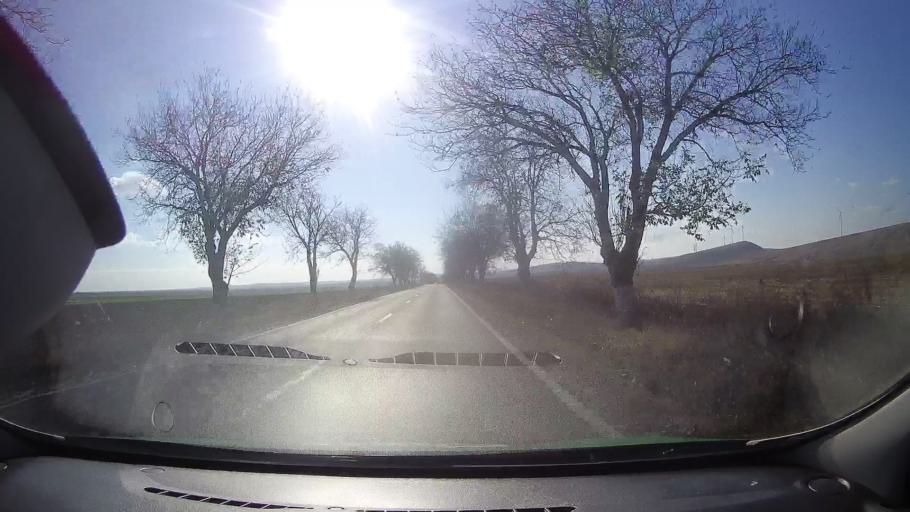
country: RO
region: Tulcea
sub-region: Comuna Ceamurlia de Jos
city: Ceamurlia de Jos
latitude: 44.7881
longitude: 28.6897
